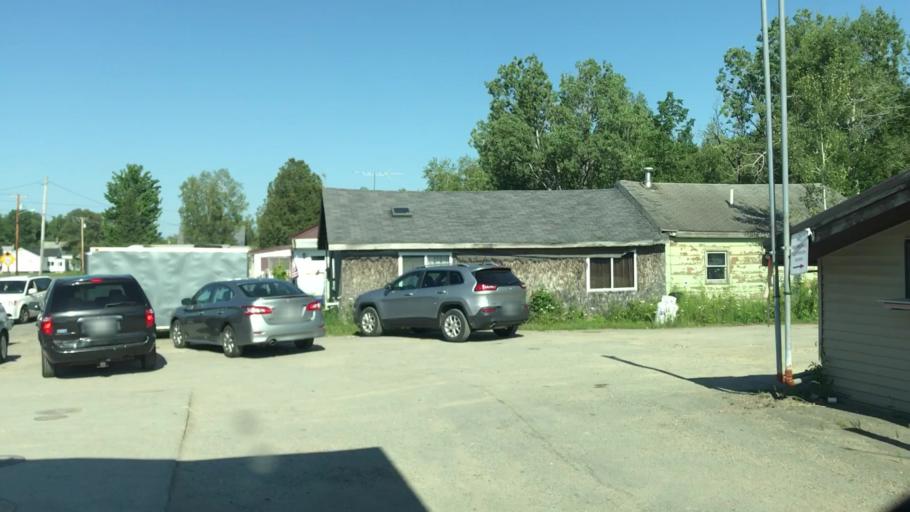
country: US
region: Maine
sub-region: Penobscot County
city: Howland
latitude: 45.2370
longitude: -68.6716
